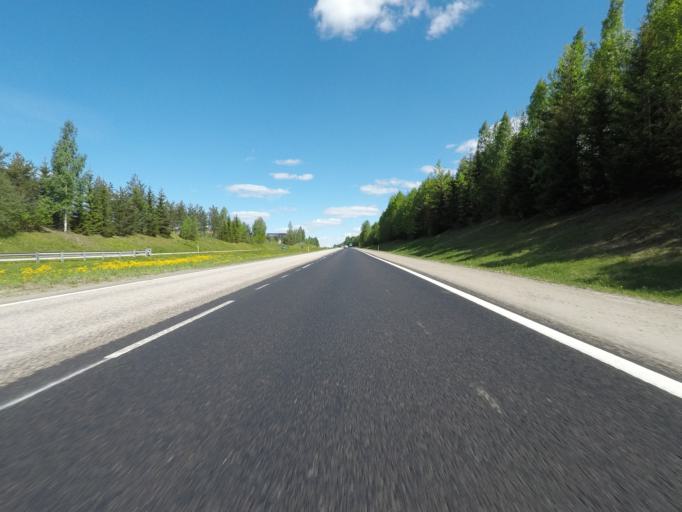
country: FI
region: Uusimaa
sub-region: Helsinki
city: Nurmijaervi
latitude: 60.4370
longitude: 24.8340
